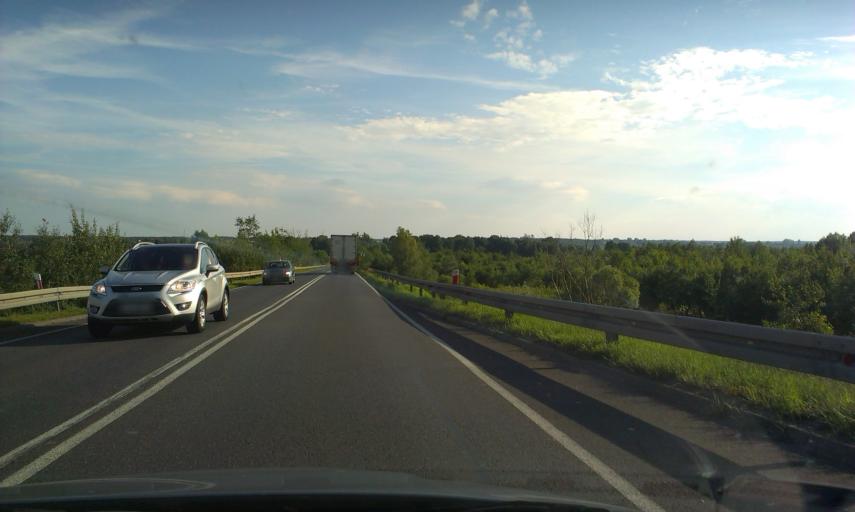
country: PL
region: Kujawsko-Pomorskie
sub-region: Powiat bydgoski
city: Biale Blota
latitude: 53.1521
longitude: 17.8859
